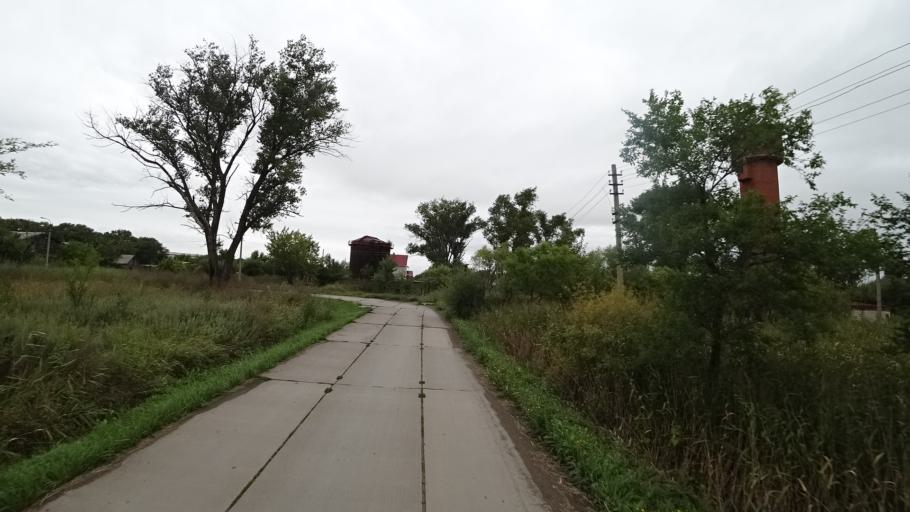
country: RU
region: Primorskiy
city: Chernigovka
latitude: 44.3344
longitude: 132.5387
